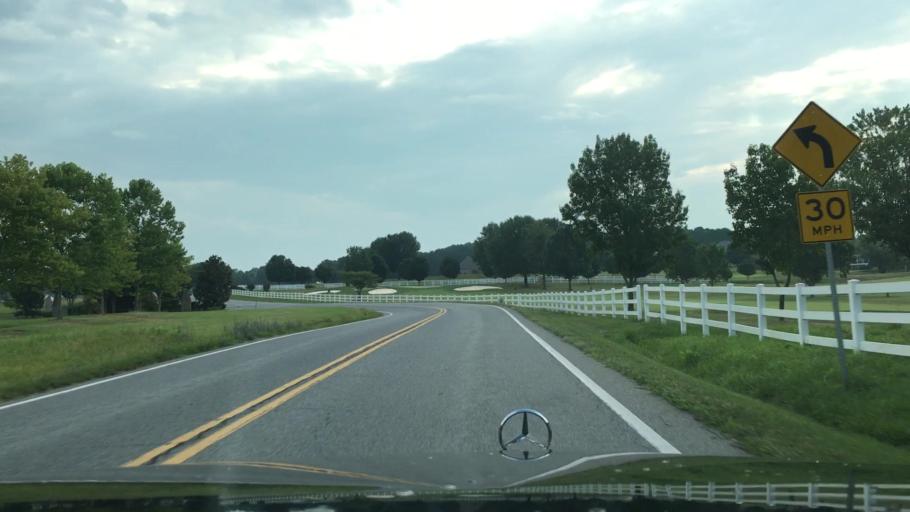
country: US
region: Virginia
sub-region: Campbell County
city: Timberlake
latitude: 37.2913
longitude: -79.3147
